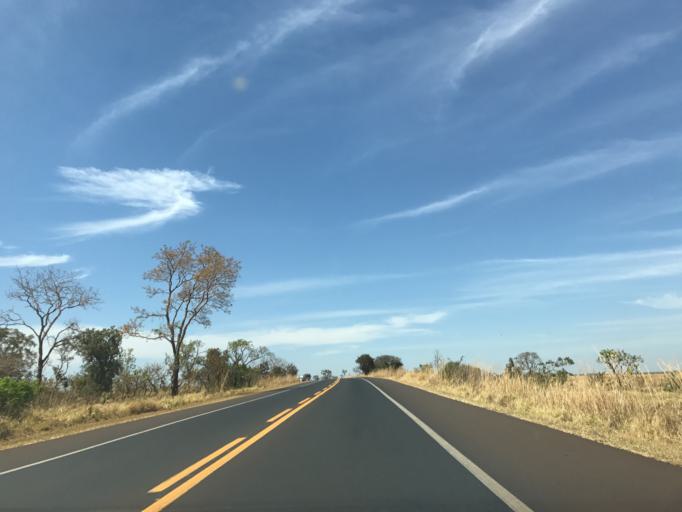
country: BR
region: Minas Gerais
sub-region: Monte Alegre De Minas
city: Monte Alegre de Minas
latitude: -19.0090
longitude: -49.0181
